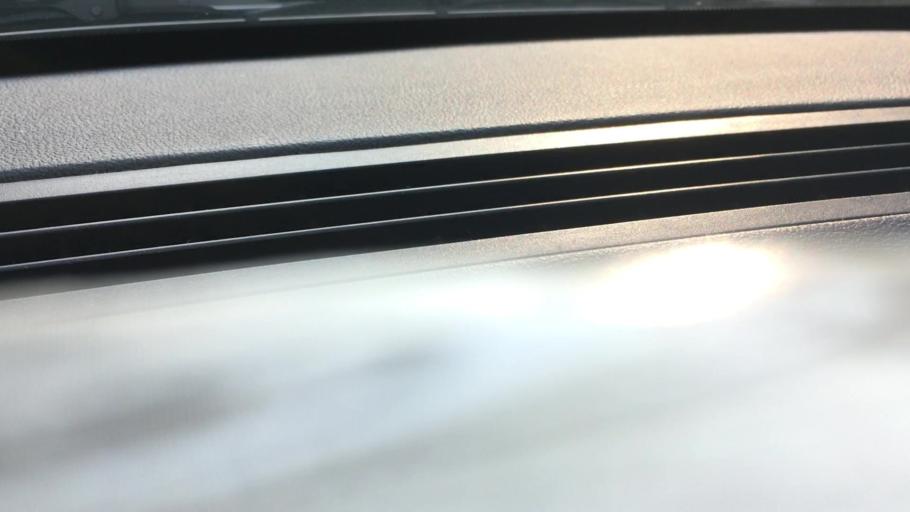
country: US
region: Alabama
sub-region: Shelby County
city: Helena
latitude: 33.2417
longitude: -86.9629
